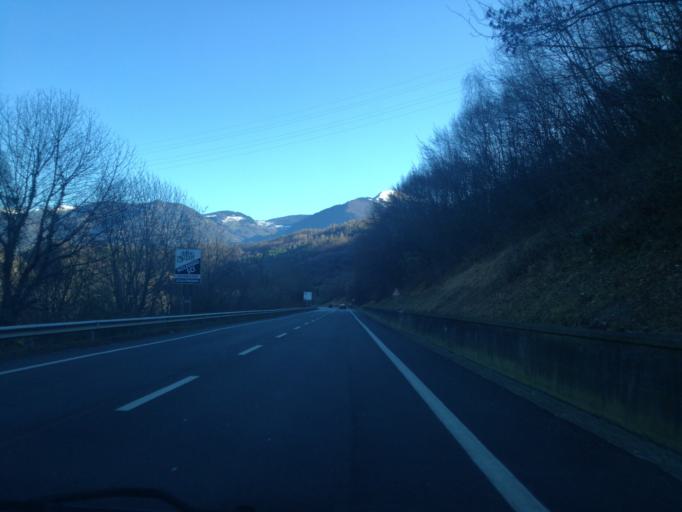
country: IT
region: Lombardy
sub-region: Provincia di Bergamo
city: Pianico
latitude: 45.8059
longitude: 10.0409
